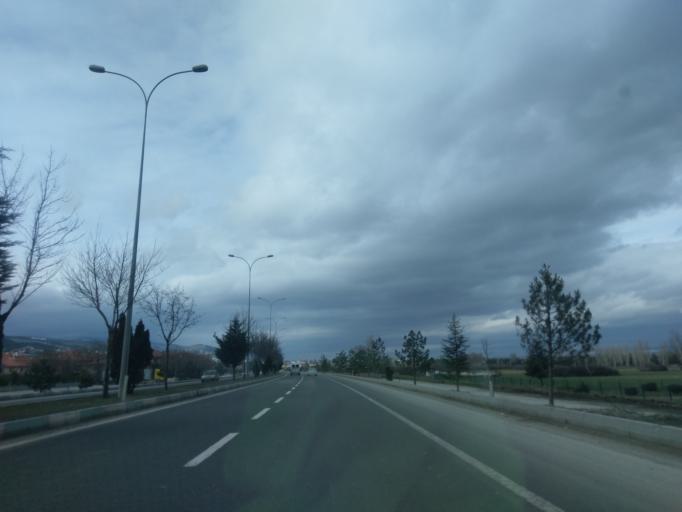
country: TR
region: Kuetahya
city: Kutahya
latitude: 39.4107
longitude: 30.0197
